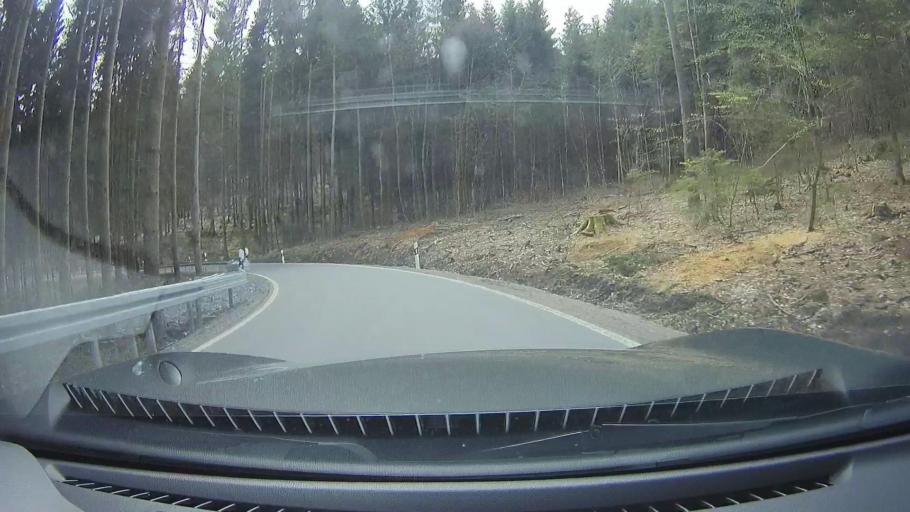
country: DE
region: Bavaria
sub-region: Regierungsbezirk Unterfranken
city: Kirchzell
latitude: 49.6273
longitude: 9.1202
